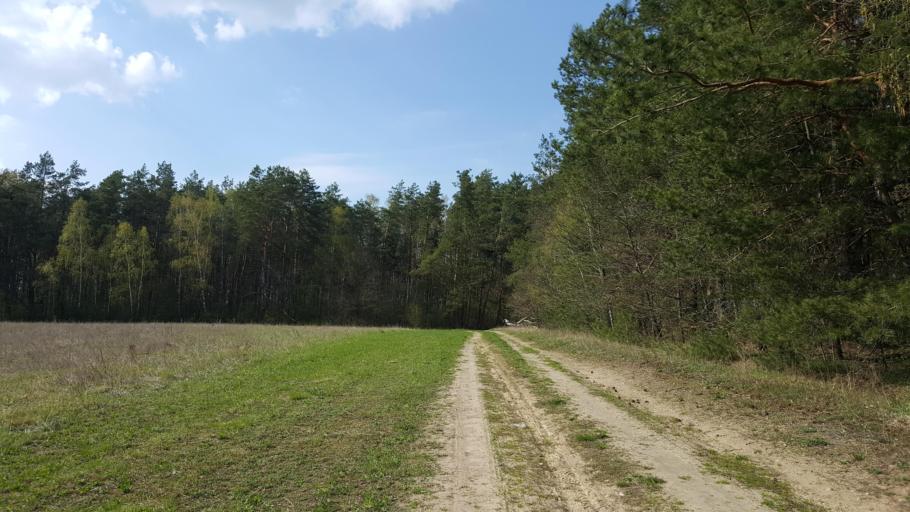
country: BY
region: Brest
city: Kamyanyets
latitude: 52.3281
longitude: 23.8538
